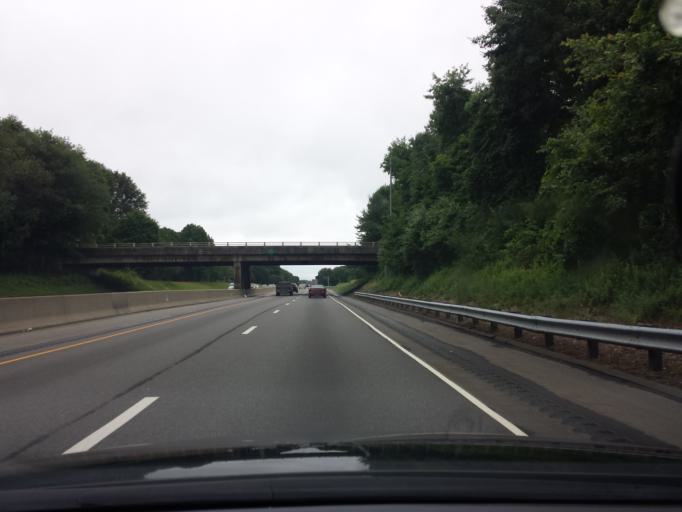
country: US
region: Connecticut
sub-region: New Haven County
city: Guilford Center
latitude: 41.2885
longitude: -72.6392
